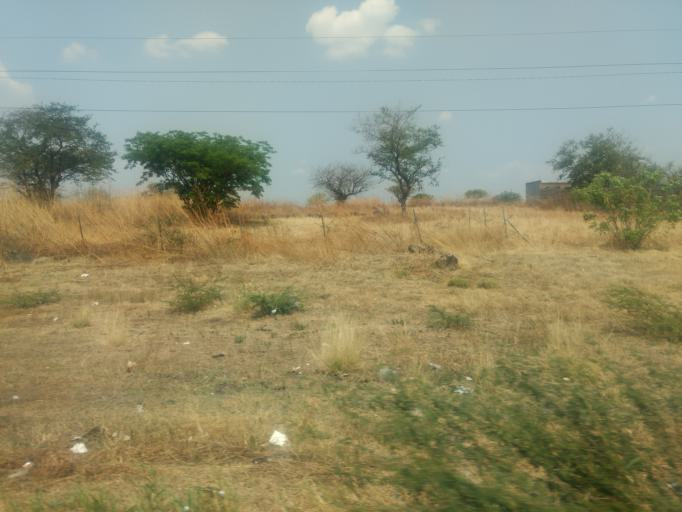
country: MX
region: Morelos
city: Alpuyeca
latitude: 18.7109
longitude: -99.2734
